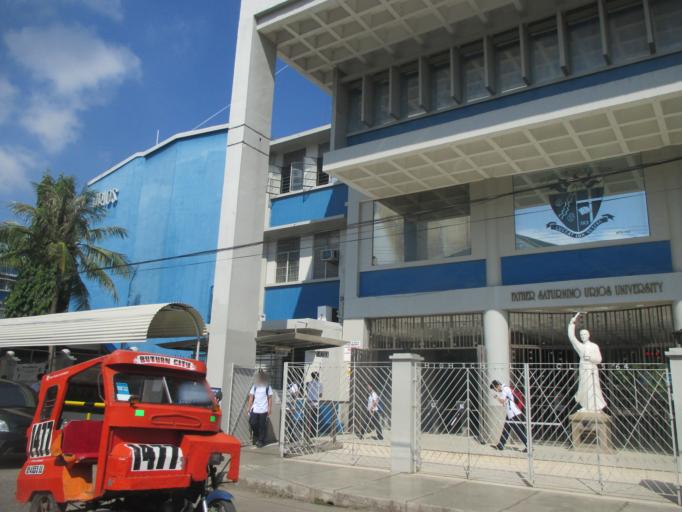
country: PH
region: Caraga
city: Butuan
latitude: 8.9478
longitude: 125.5422
